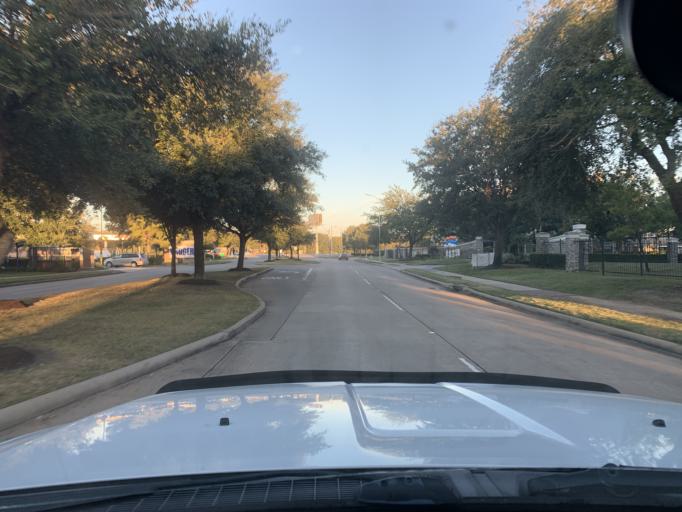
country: US
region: Texas
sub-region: Fort Bend County
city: Four Corners
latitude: 29.6489
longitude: -95.6489
